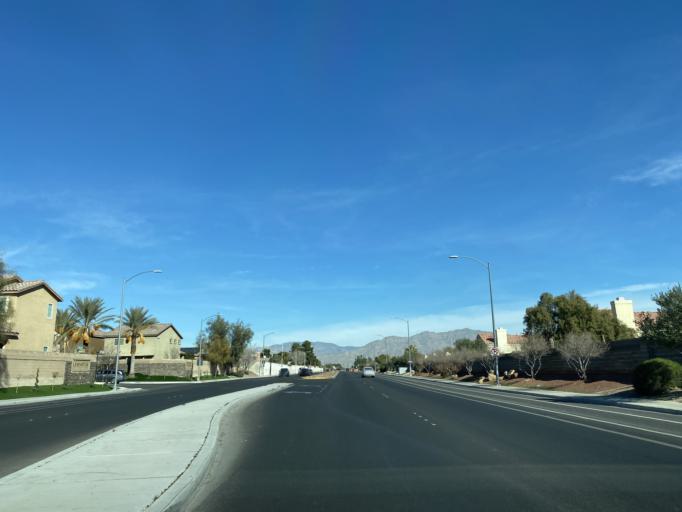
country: US
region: Nevada
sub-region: Clark County
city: Las Vegas
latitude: 36.2416
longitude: -115.2255
